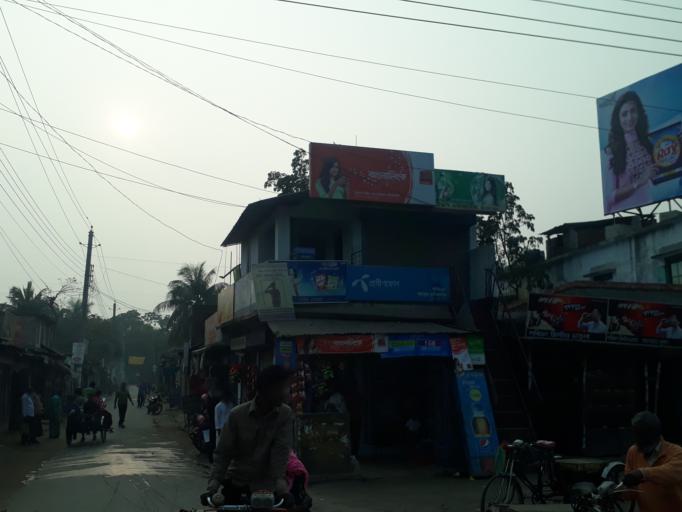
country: BD
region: Khulna
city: Bhatpara Abhaynagar
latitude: 22.9477
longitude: 89.4796
